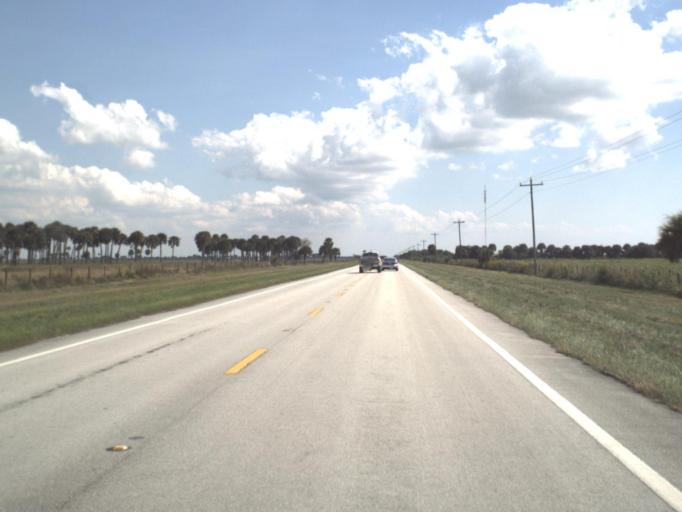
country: US
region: Florida
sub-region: Okeechobee County
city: Okeechobee
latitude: 27.3555
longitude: -80.9589
